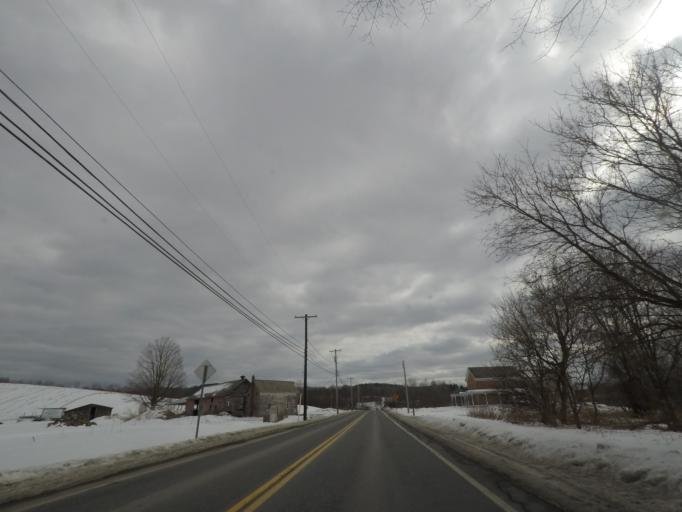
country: US
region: New York
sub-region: Washington County
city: Greenwich
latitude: 43.0834
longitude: -73.4862
